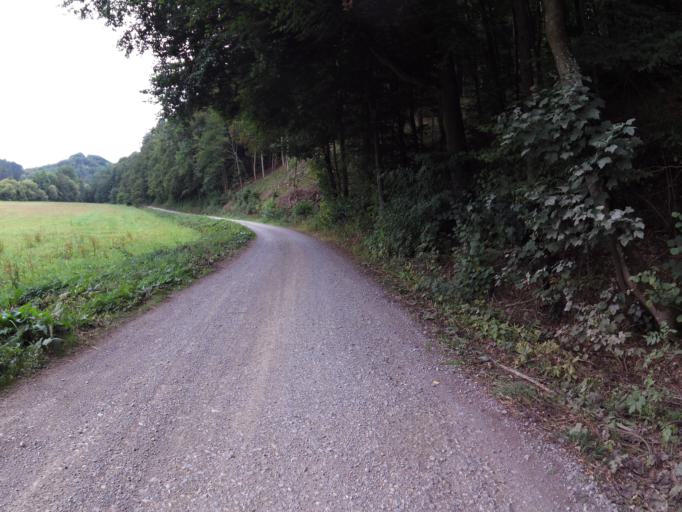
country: DE
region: North Rhine-Westphalia
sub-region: Regierungsbezirk Koln
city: Nettersheim
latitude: 50.5099
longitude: 6.6177
